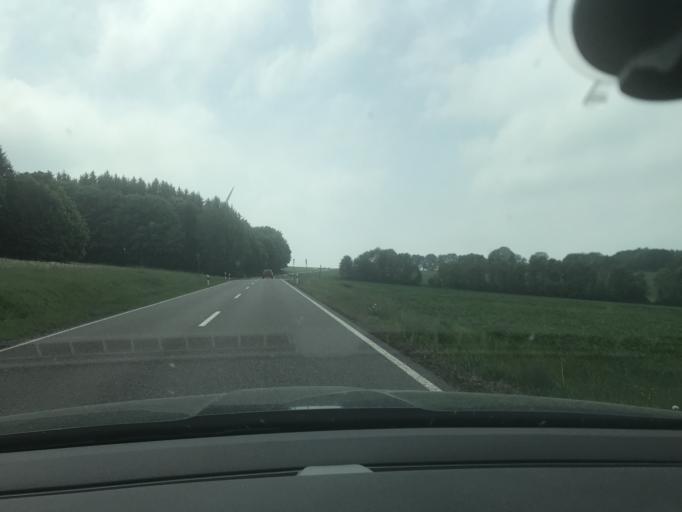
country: DE
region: Saxony
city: Grosshartmannsdorf
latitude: 50.7483
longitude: 13.2961
